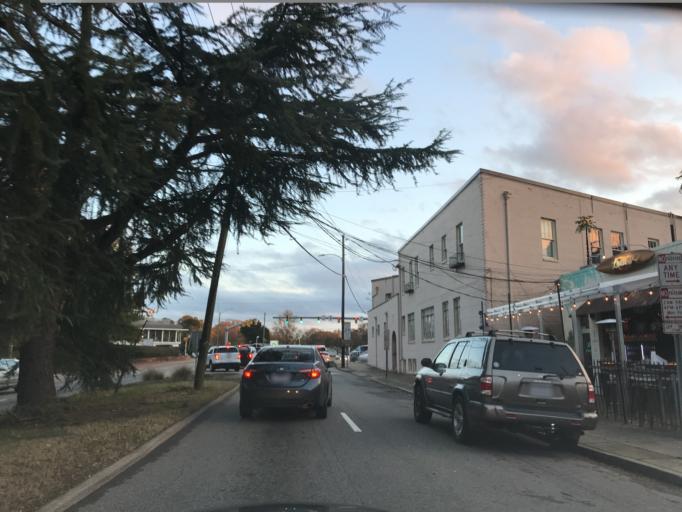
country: US
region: North Carolina
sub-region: Wake County
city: West Raleigh
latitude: 35.8049
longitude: -78.6464
